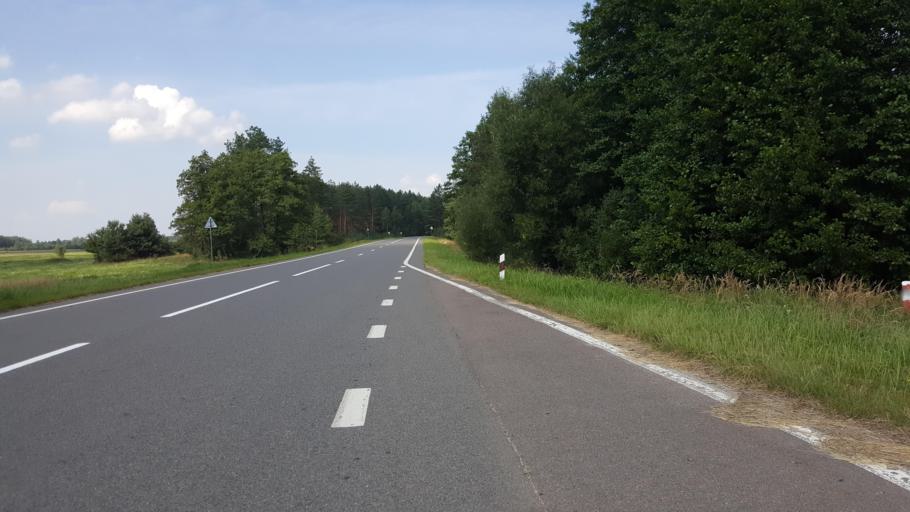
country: BY
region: Brest
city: Kamyanyuki
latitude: 52.5593
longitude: 23.6278
